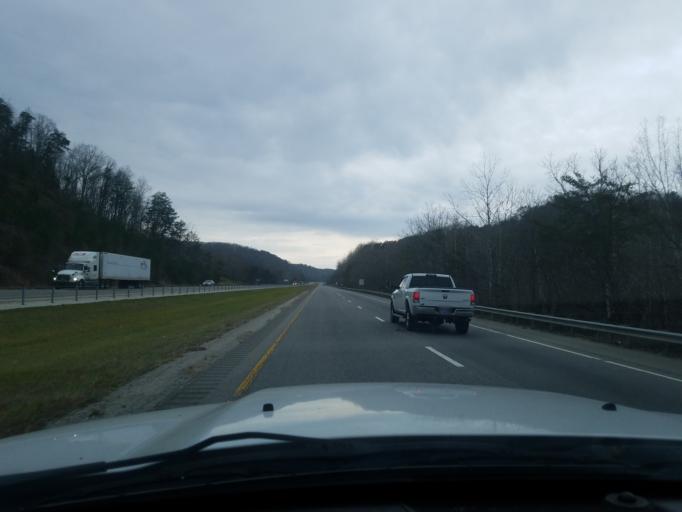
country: US
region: Kentucky
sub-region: Boyd County
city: Meads
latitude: 38.3652
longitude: -82.7830
